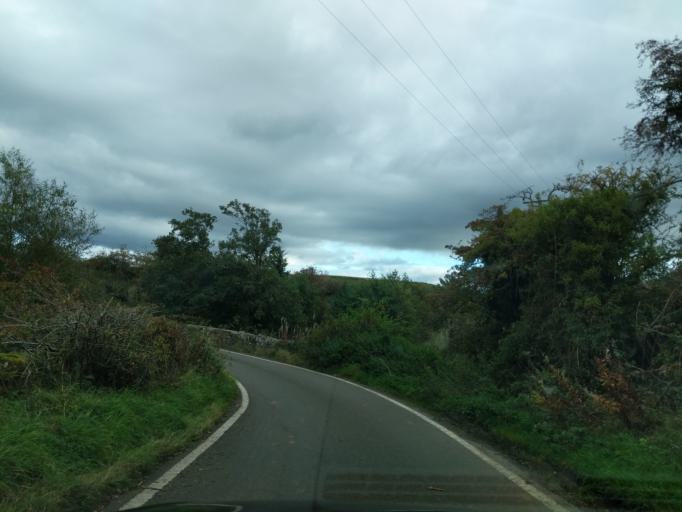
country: GB
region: Scotland
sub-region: East Lothian
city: East Linton
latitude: 55.9399
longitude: -2.7092
